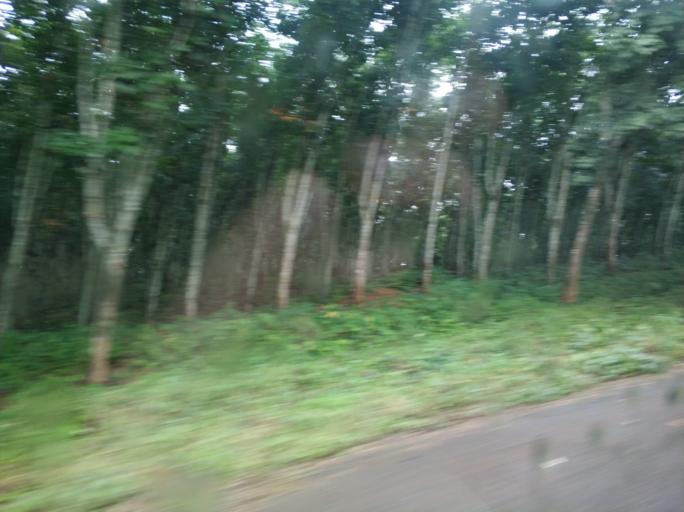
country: NG
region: Ogun
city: Abigi
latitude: 6.7076
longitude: 4.4598
